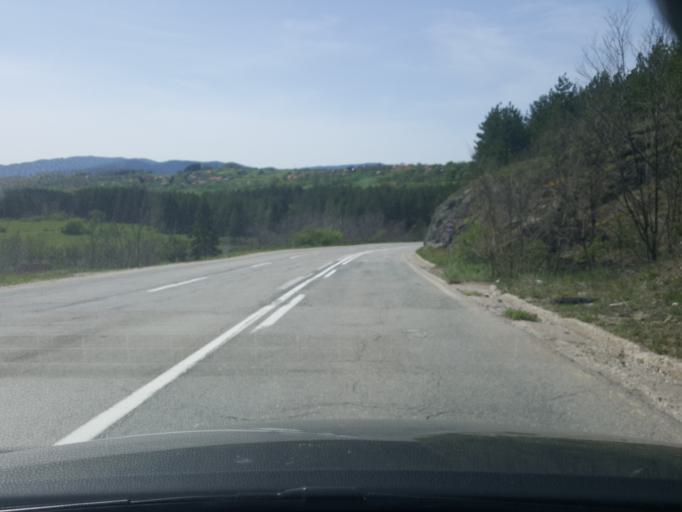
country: RS
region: Central Serbia
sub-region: Zlatiborski Okrug
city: Cajetina
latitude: 43.8352
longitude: 19.6082
